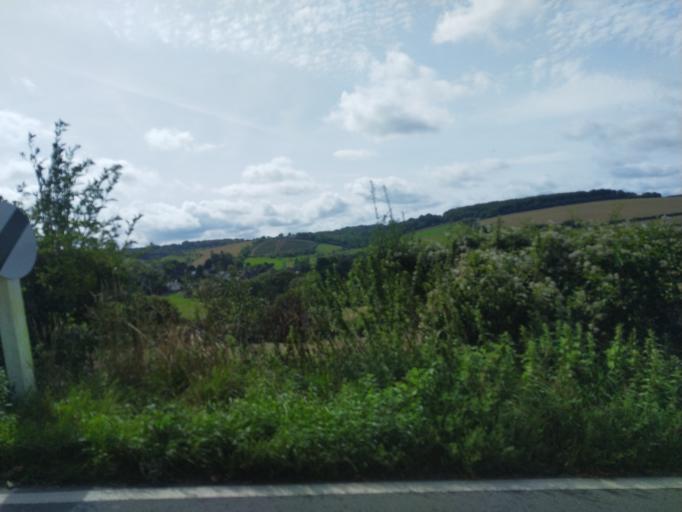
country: GB
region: England
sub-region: Dorset
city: Blandford Forum
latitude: 50.8805
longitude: -2.1958
